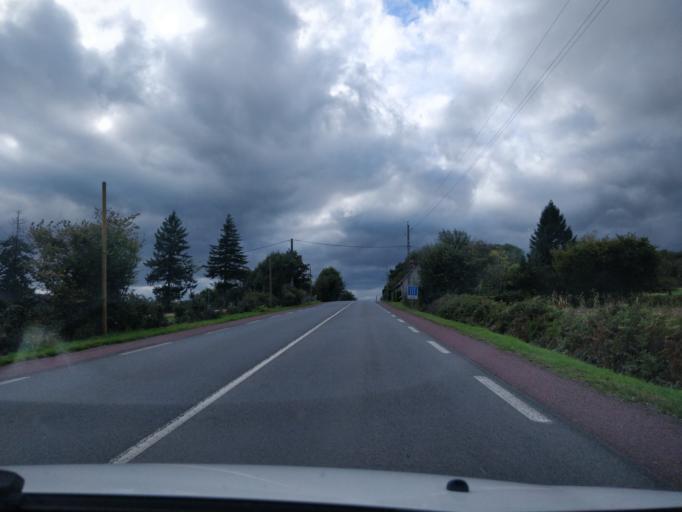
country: FR
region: Lower Normandy
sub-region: Departement du Calvados
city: Saint-Sever-Calvados
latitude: 48.8398
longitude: -1.0024
